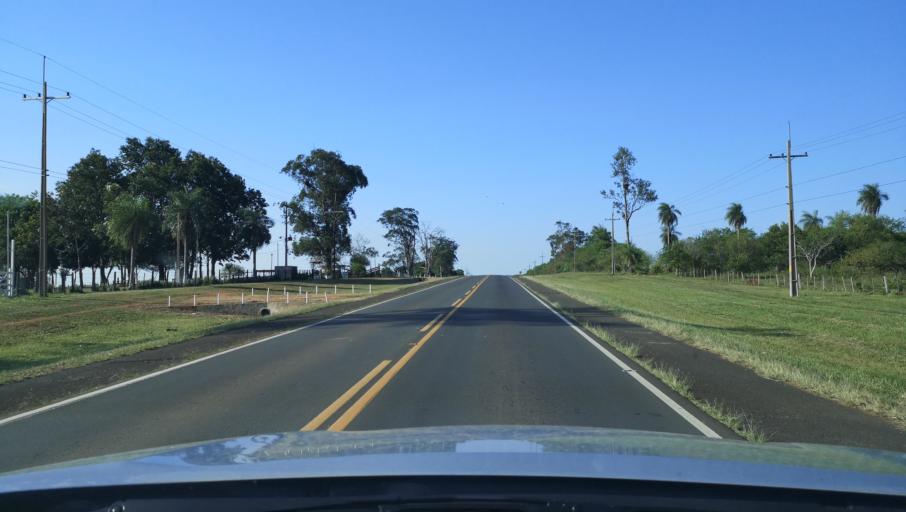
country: PY
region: Misiones
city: Santa Maria
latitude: -26.8242
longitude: -57.0281
